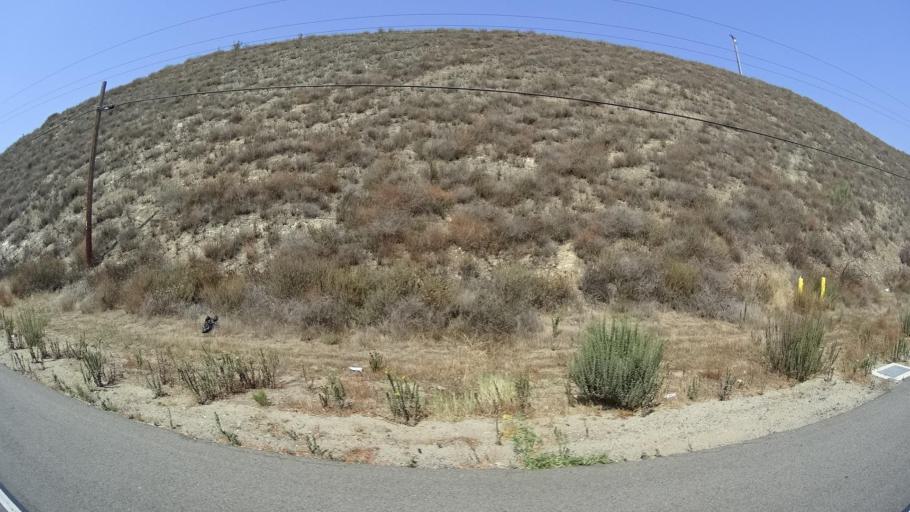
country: US
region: California
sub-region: San Diego County
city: Bonsall
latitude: 33.2699
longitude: -117.2365
